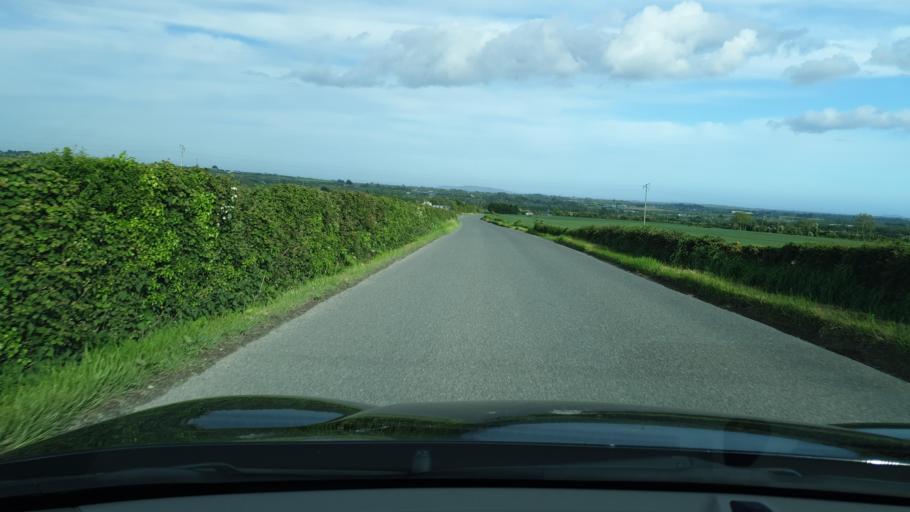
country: IE
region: Leinster
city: Balrothery
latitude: 53.5519
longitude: -6.2350
